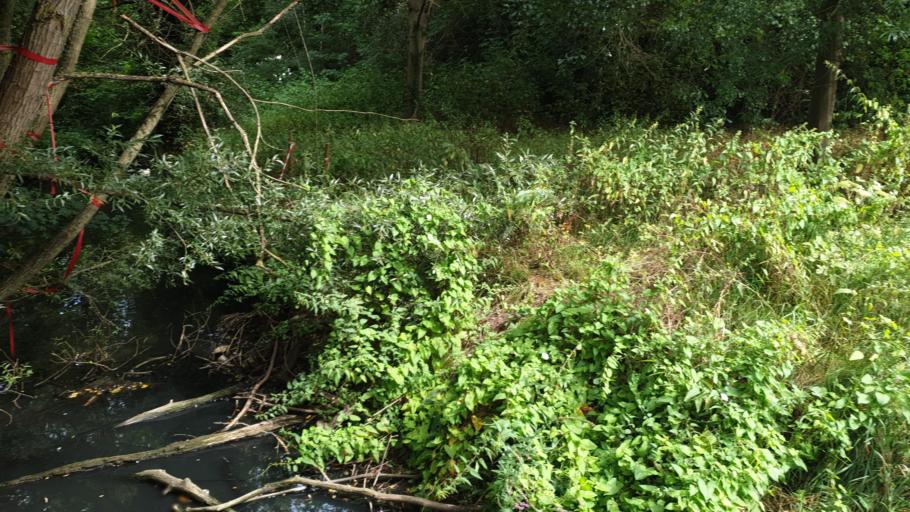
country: BE
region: Flanders
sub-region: Provincie Oost-Vlaanderen
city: Aalst
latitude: 50.9838
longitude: 4.0542
